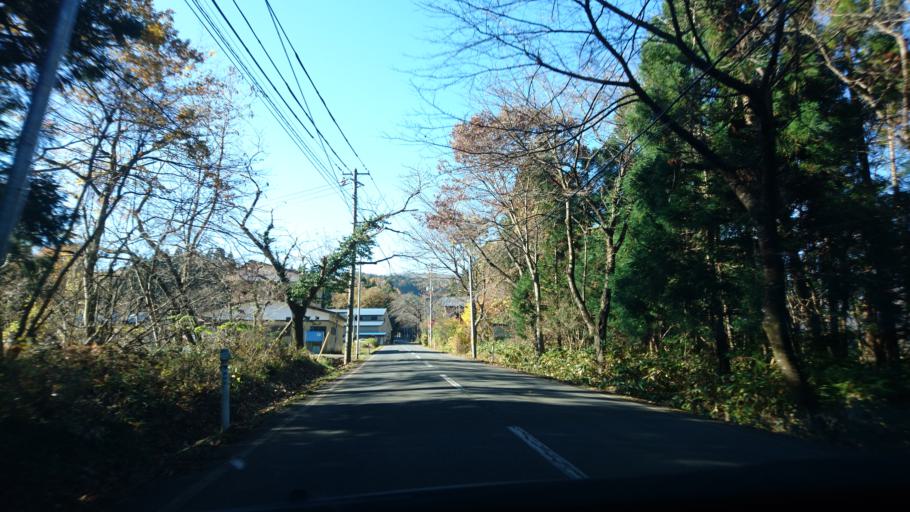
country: JP
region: Iwate
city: Mizusawa
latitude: 39.1177
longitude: 140.9503
